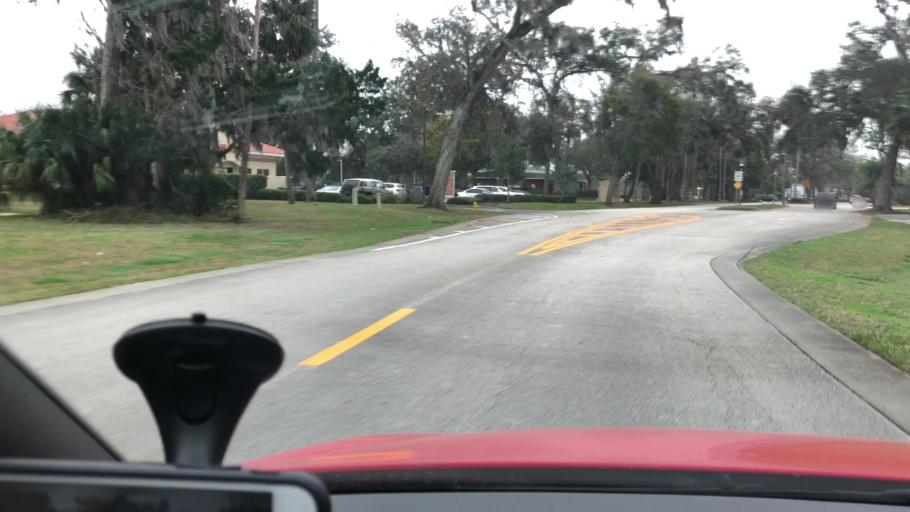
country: US
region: Florida
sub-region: Volusia County
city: Port Orange
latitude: 29.1279
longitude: -81.0085
